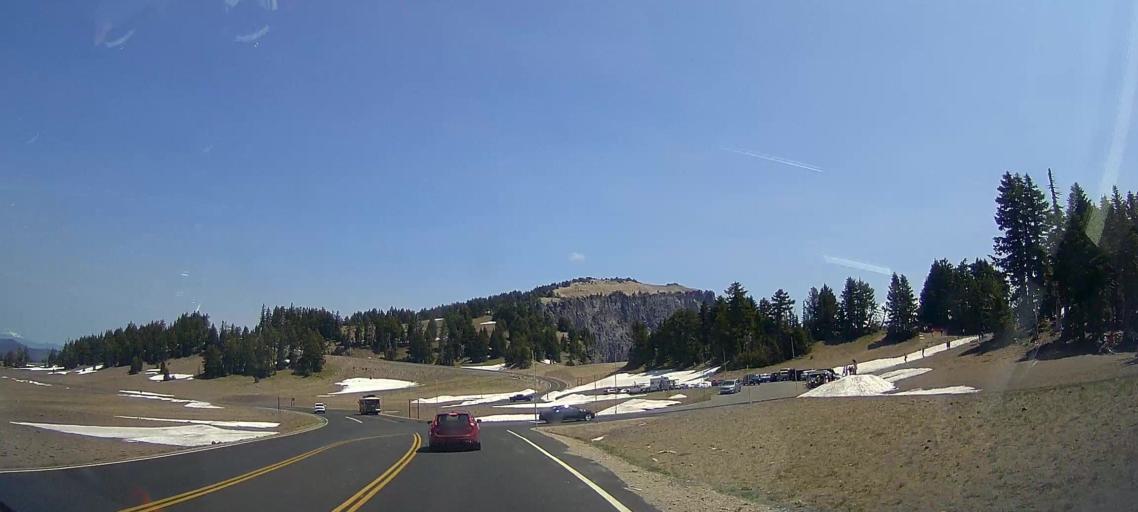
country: US
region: Oregon
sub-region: Jackson County
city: Shady Cove
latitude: 42.9636
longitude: -122.1535
